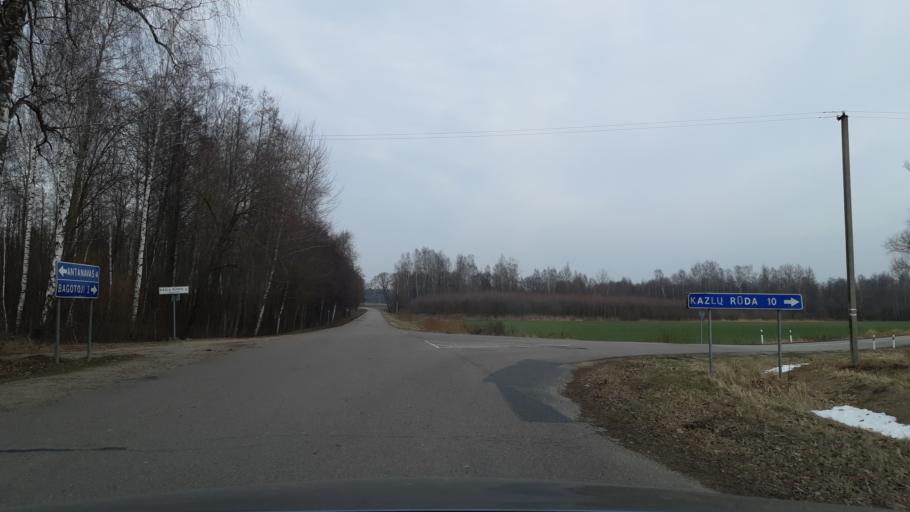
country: LT
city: Kazlu Ruda
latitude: 54.7326
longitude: 23.3404
